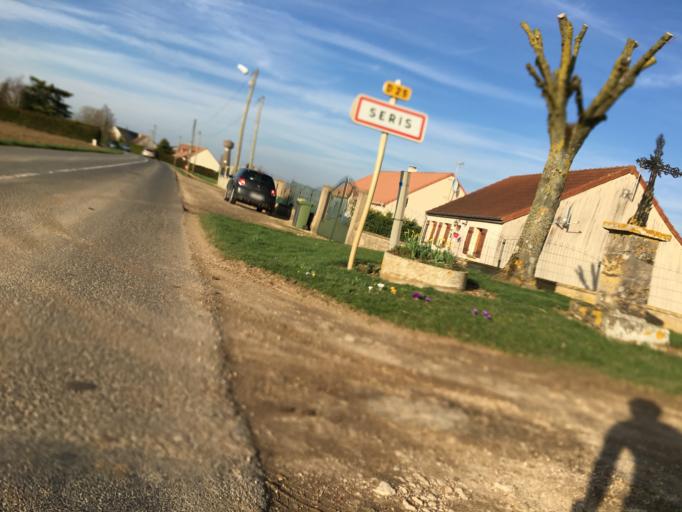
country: FR
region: Centre
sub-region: Departement du Loir-et-Cher
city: Mer
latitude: 47.7533
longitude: 1.5047
